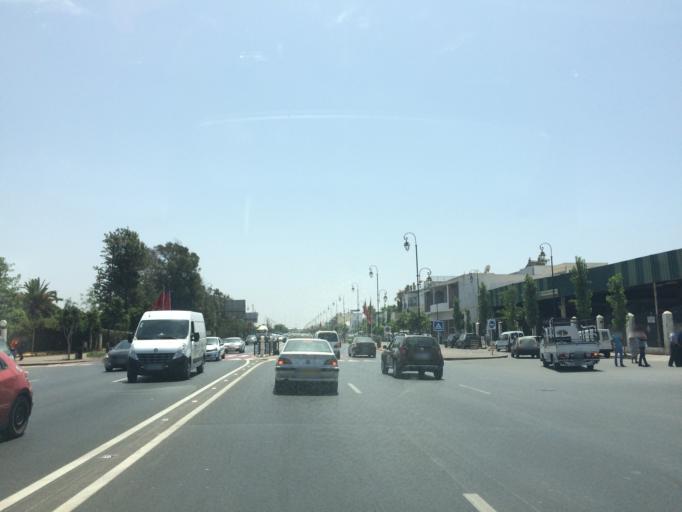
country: MA
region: Rabat-Sale-Zemmour-Zaer
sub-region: Rabat
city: Rabat
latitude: 33.9900
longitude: -6.8670
